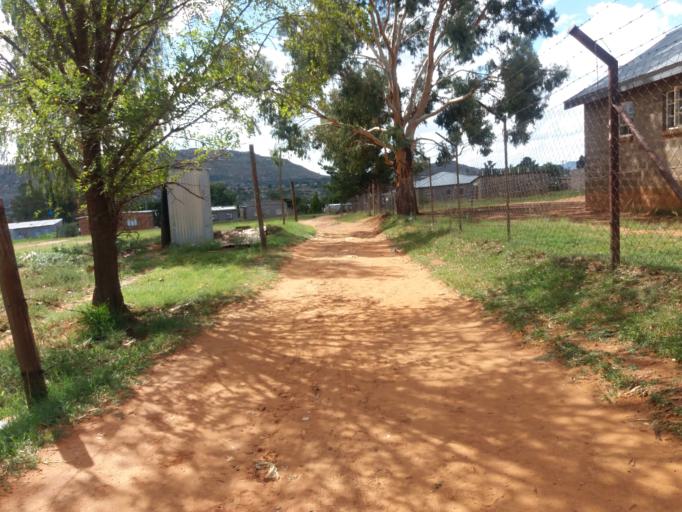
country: LS
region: Maseru
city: Maseru
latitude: -29.3697
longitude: 27.5065
